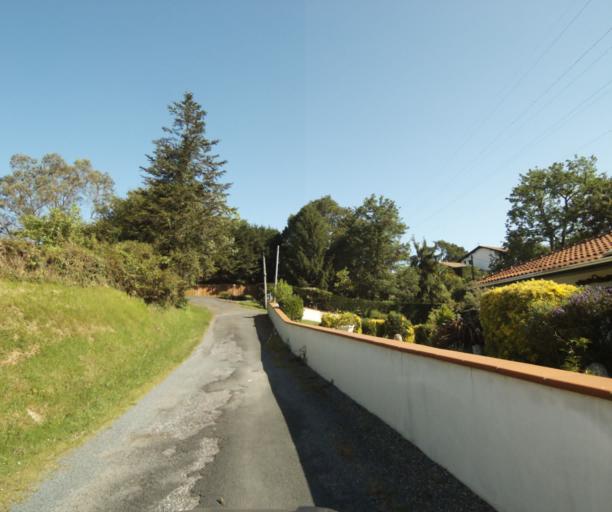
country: FR
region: Aquitaine
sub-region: Departement des Pyrenees-Atlantiques
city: Mouguerre
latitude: 43.4684
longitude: -1.4377
